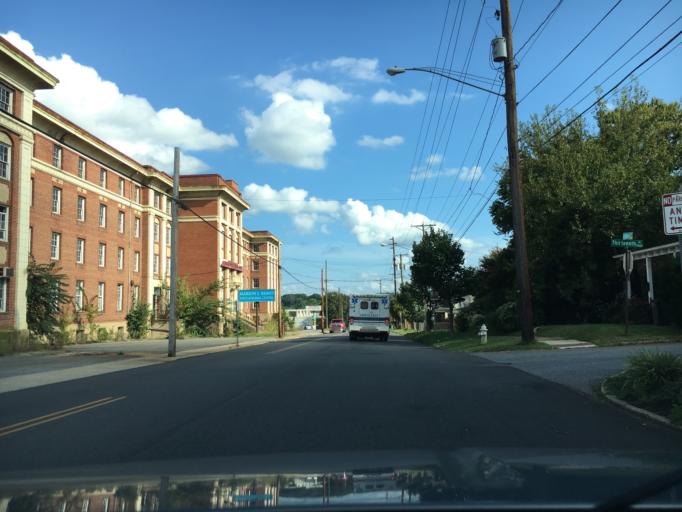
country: US
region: Virginia
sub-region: City of Lynchburg
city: Lynchburg
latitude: 37.4020
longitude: -79.1569
